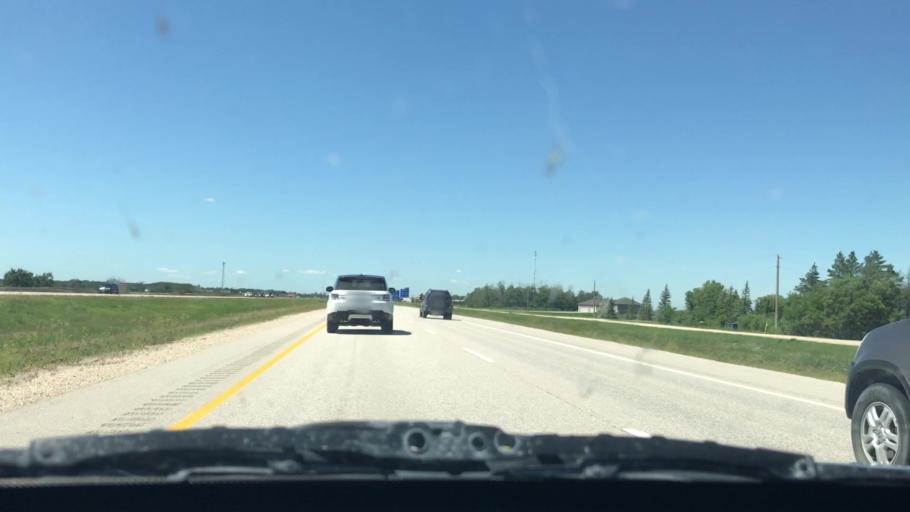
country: CA
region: Manitoba
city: Winnipeg
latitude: 49.8147
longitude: -96.9220
